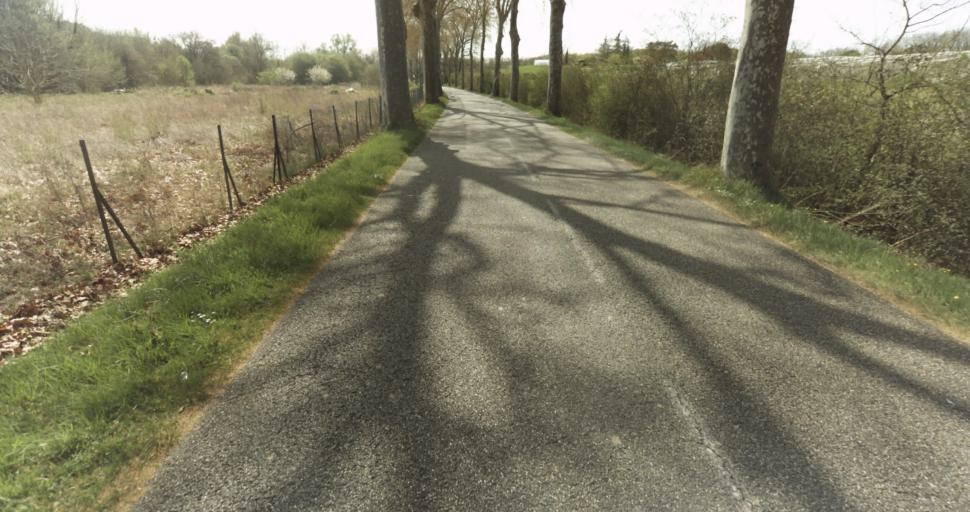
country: FR
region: Midi-Pyrenees
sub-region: Departement du Tarn-et-Garonne
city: Moissac
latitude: 44.1594
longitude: 1.1131
